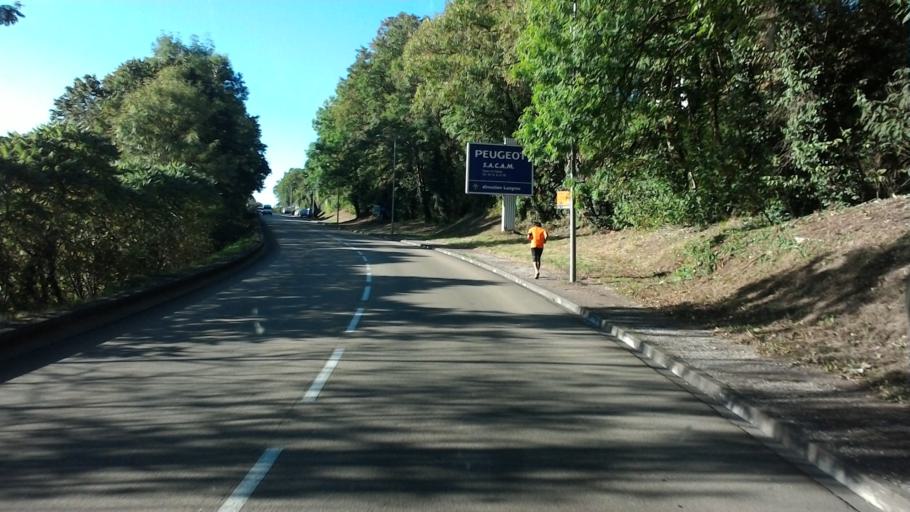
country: FR
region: Champagne-Ardenne
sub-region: Departement de la Haute-Marne
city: Chaumont
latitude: 48.1213
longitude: 5.1433
